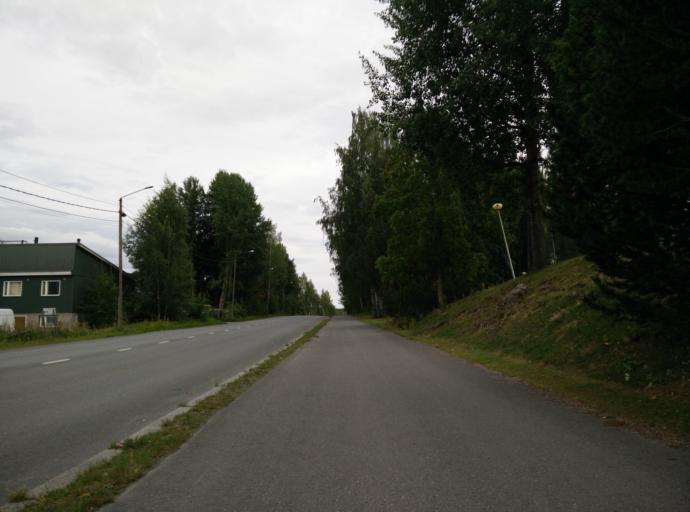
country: FI
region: Haeme
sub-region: Haemeenlinna
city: Haemeenlinna
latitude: 60.9906
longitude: 24.4939
